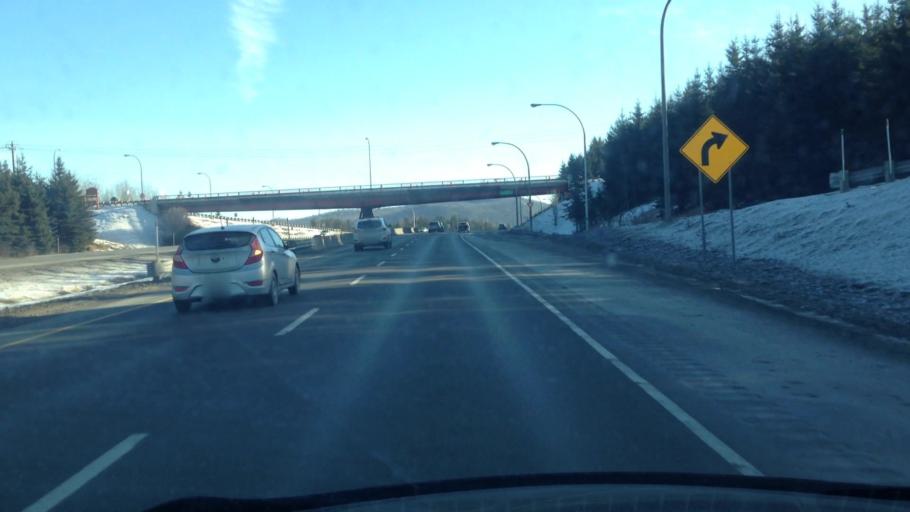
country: CA
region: Quebec
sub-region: Laurentides
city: Prevost
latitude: 45.8861
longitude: -74.1231
